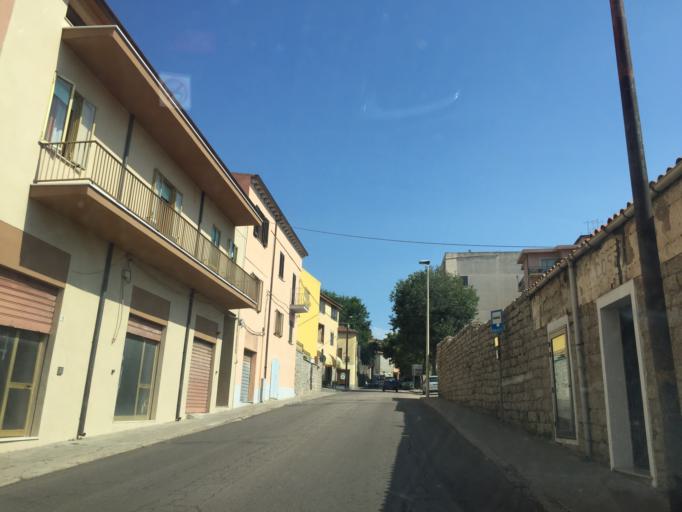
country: IT
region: Sardinia
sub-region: Provincia di Olbia-Tempio
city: Tempio Pausania
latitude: 40.9047
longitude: 9.1006
